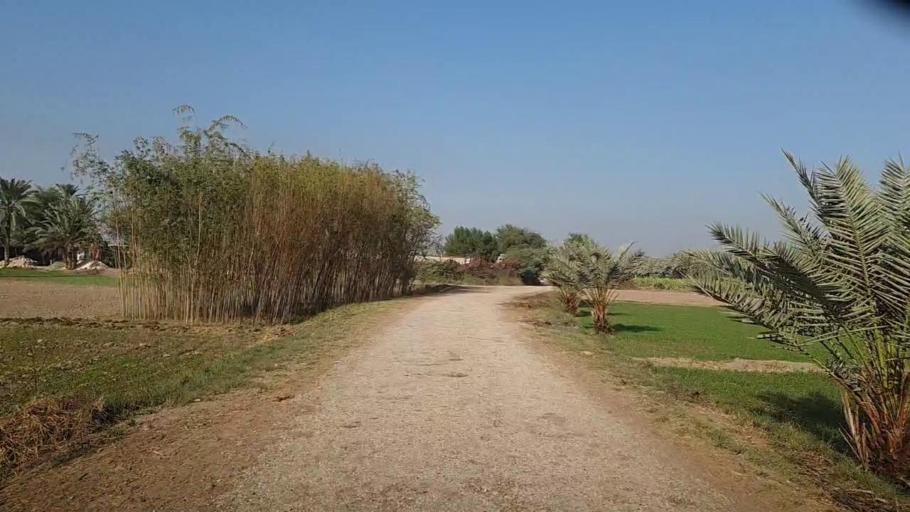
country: PK
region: Sindh
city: Ranipur
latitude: 27.2529
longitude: 68.5504
